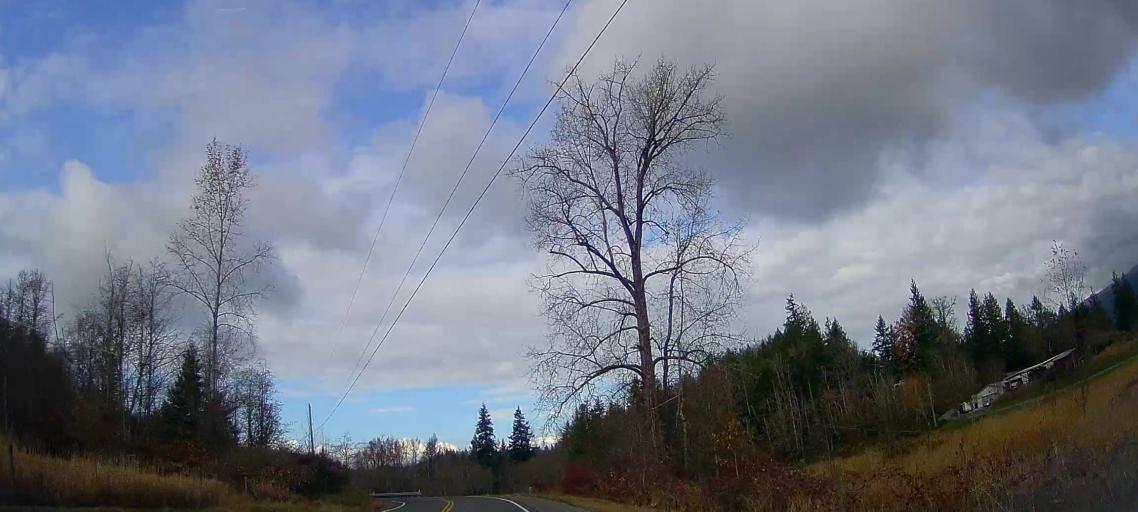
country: US
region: Washington
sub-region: Skagit County
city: Big Lake
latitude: 48.4064
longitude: -122.2161
